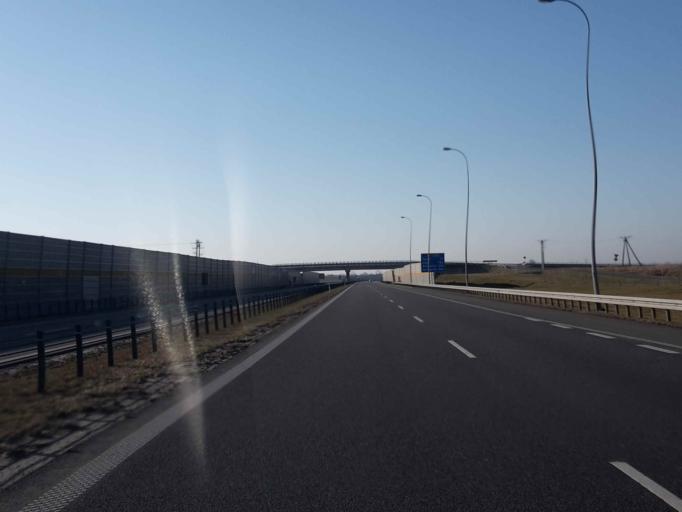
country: PL
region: Kujawsko-Pomorskie
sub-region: Powiat torunski
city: Lubicz Dolny
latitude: 53.0837
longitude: 18.7507
